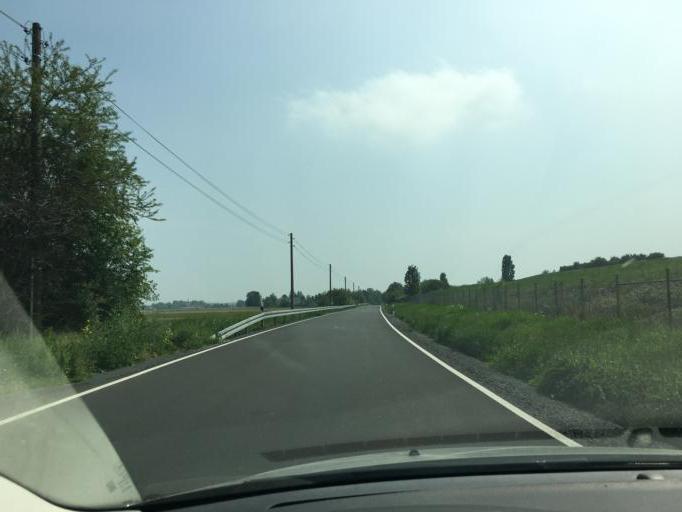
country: DE
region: Saxony
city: Grossposna
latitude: 51.2954
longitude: 12.4955
